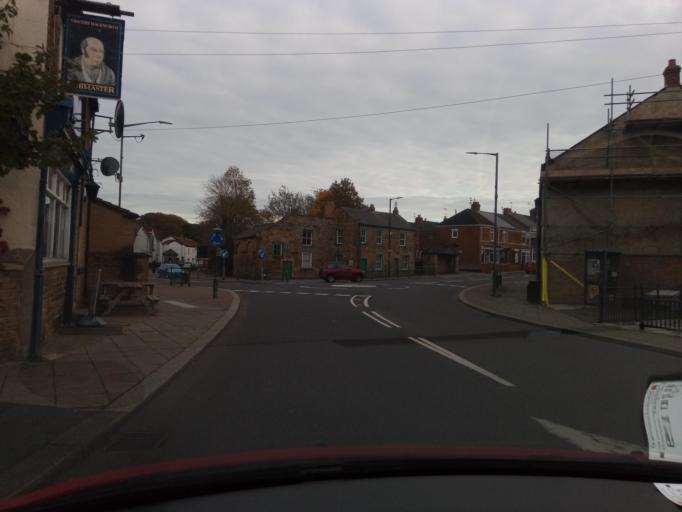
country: GB
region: England
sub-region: County Durham
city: Shildon
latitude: 54.6324
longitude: -1.6547
